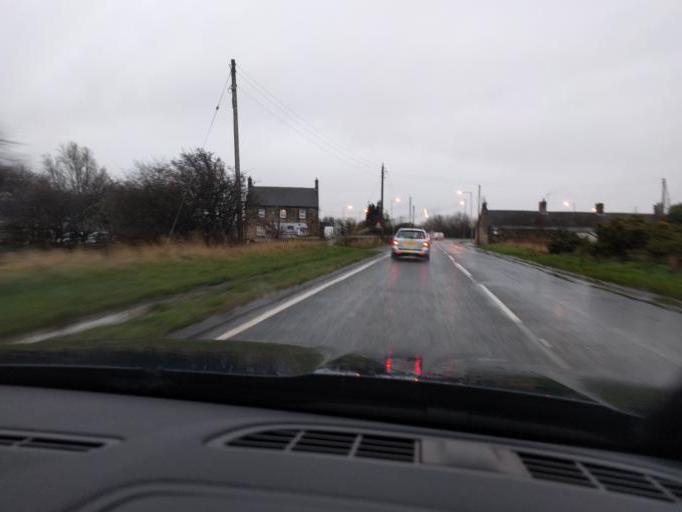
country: GB
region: England
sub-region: Northumberland
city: Cramlington
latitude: 55.1017
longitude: -1.5603
